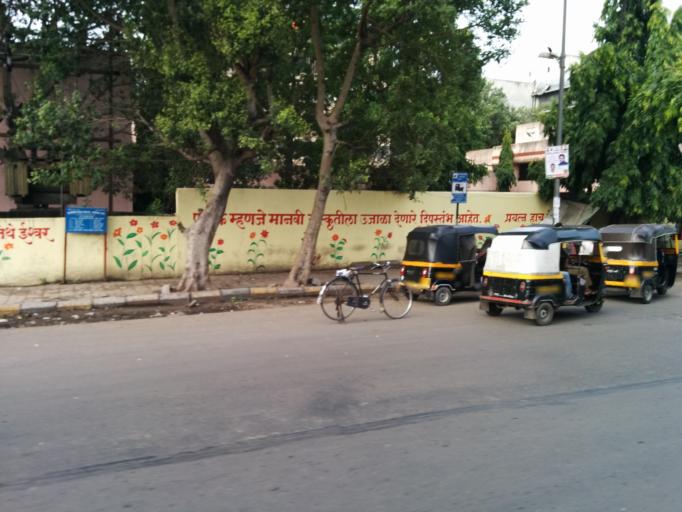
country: IN
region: Maharashtra
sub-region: Pune Division
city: Pune
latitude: 18.5065
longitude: 73.9022
